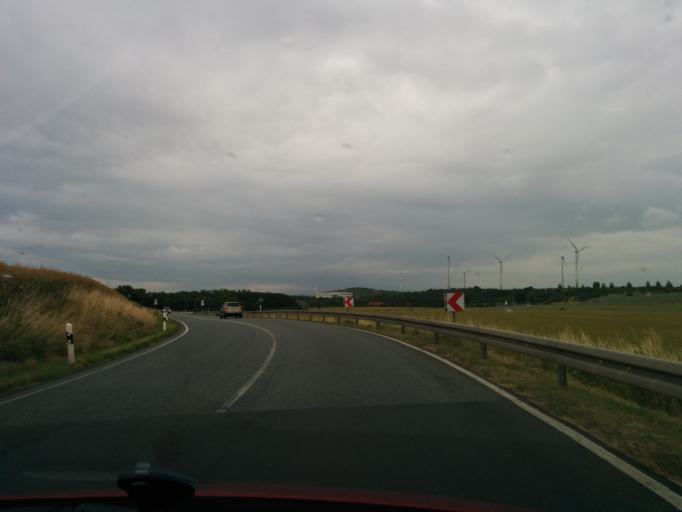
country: DE
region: Thuringia
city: Kleinfurra
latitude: 51.4453
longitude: 10.7846
